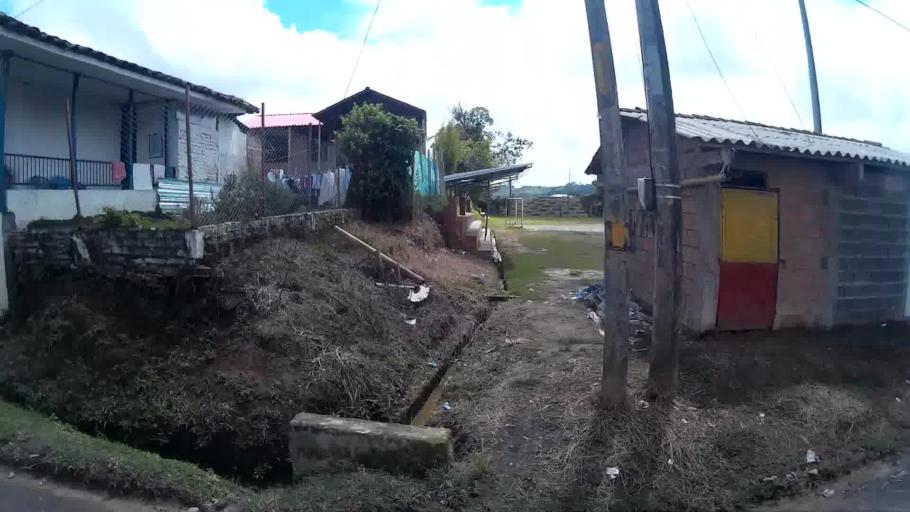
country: CO
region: Valle del Cauca
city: Ulloa
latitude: 4.7206
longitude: -75.7097
